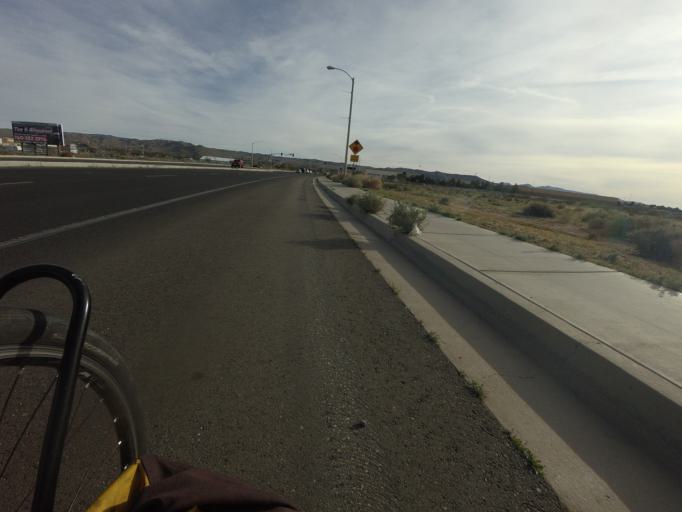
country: US
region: California
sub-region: Kern County
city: Ridgecrest
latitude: 35.6093
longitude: -117.6704
